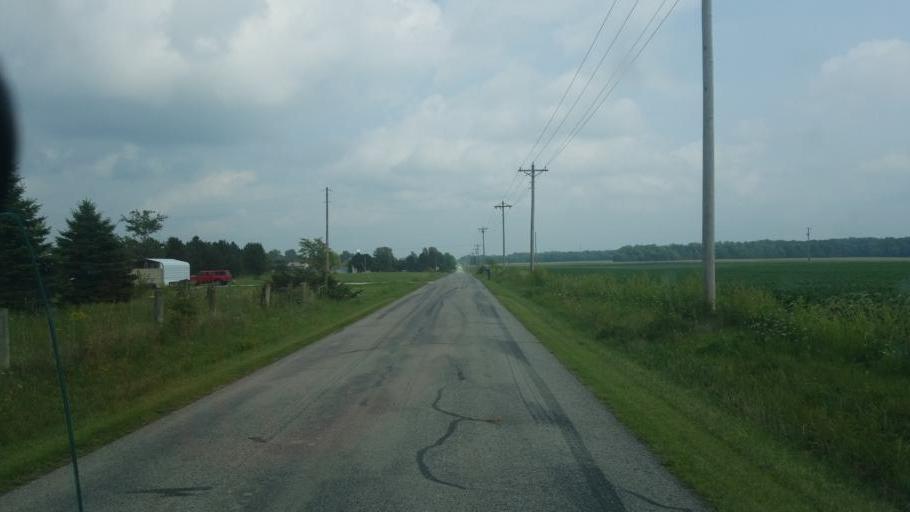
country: US
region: Ohio
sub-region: Huron County
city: Greenwich
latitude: 41.0938
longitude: -82.5154
